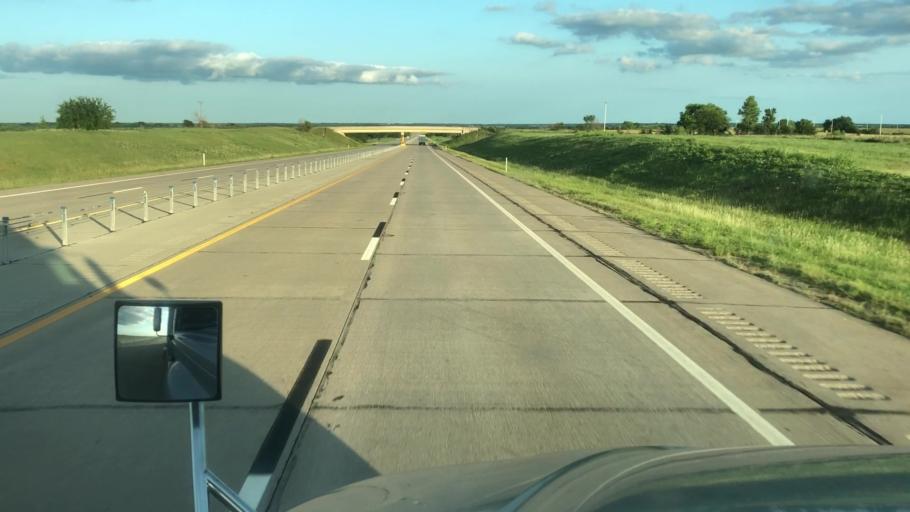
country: US
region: Oklahoma
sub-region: Pawnee County
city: Pawnee
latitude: 36.3357
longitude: -97.0182
